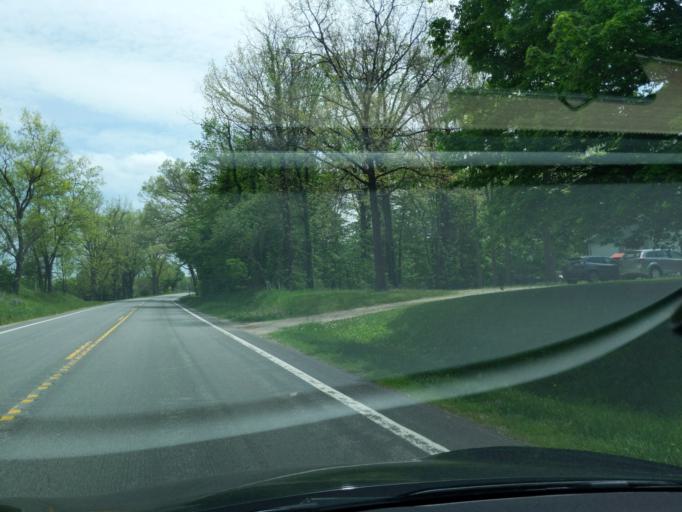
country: US
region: Michigan
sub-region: Ingham County
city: Stockbridge
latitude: 42.5058
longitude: -84.1482
